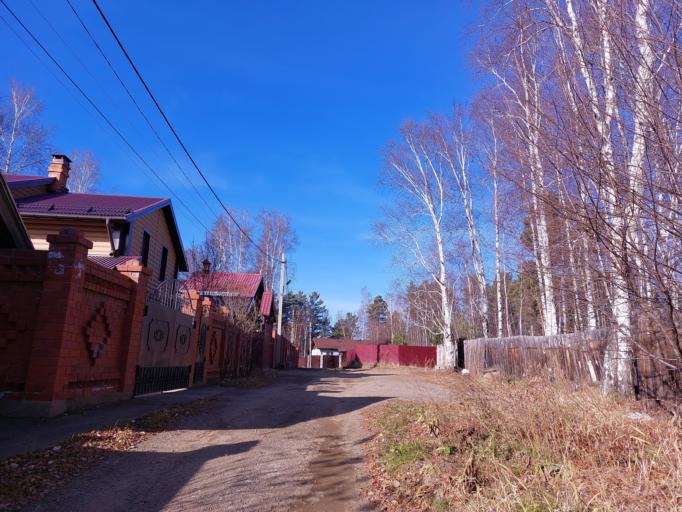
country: RU
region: Irkutsk
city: Pivovarikha
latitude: 52.1870
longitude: 104.4549
